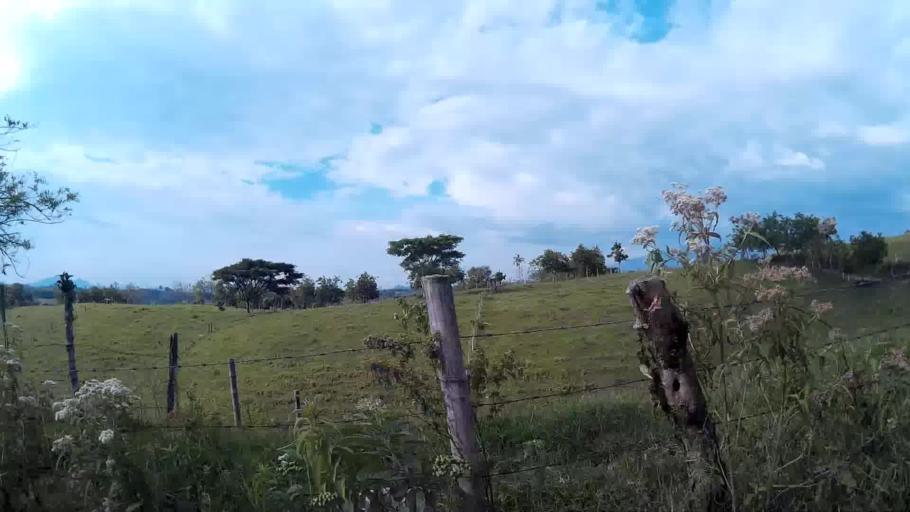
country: CO
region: Valle del Cauca
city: Ulloa
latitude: 4.7141
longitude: -75.7020
